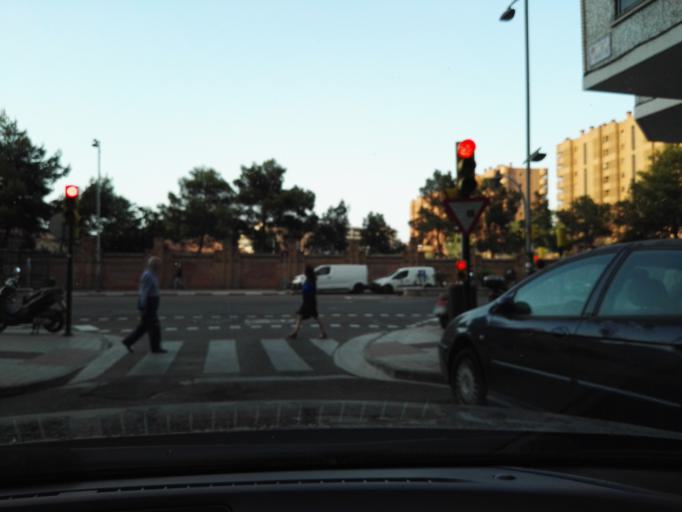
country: ES
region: Aragon
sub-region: Provincia de Zaragoza
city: Zaragoza
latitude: 41.6400
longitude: -0.8825
